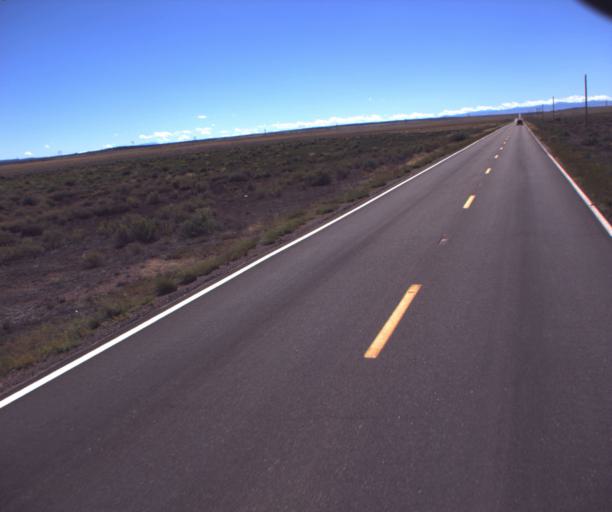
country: US
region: Arizona
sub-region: Apache County
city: Saint Johns
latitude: 34.6137
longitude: -109.3190
